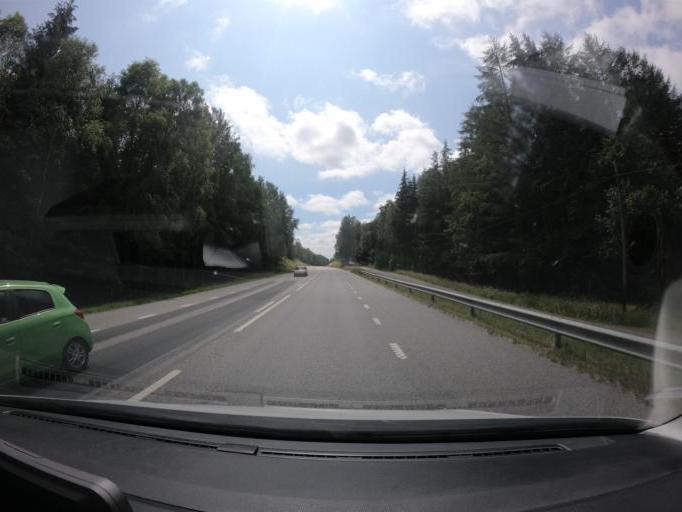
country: SE
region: Skane
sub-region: Hoors Kommun
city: Hoeoer
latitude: 55.9781
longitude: 13.5952
